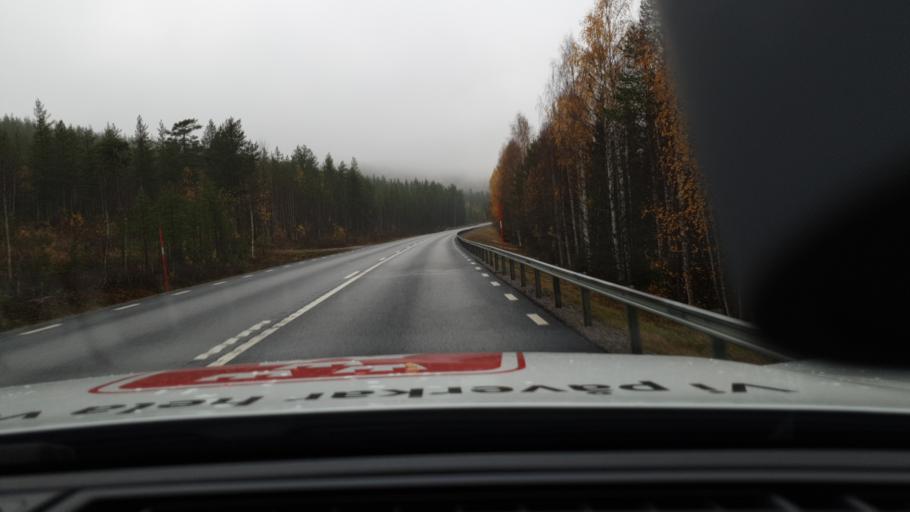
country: SE
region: Norrbotten
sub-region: Overkalix Kommun
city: OEverkalix
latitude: 66.6449
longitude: 22.1904
